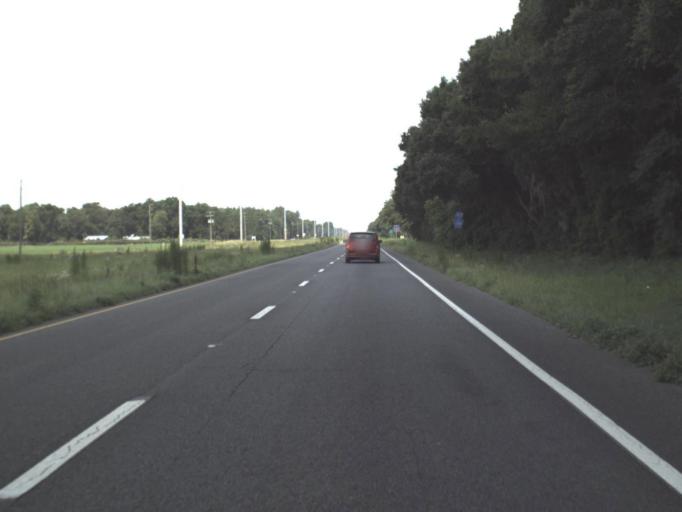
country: US
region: Florida
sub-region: Levy County
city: Chiefland
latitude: 29.4751
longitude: -82.7851
